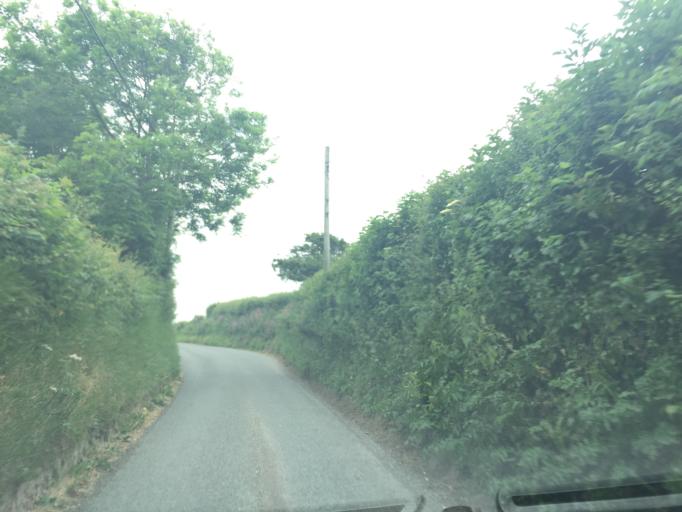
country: GB
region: England
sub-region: Dorset
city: Overcombe
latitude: 50.6446
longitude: -2.3630
